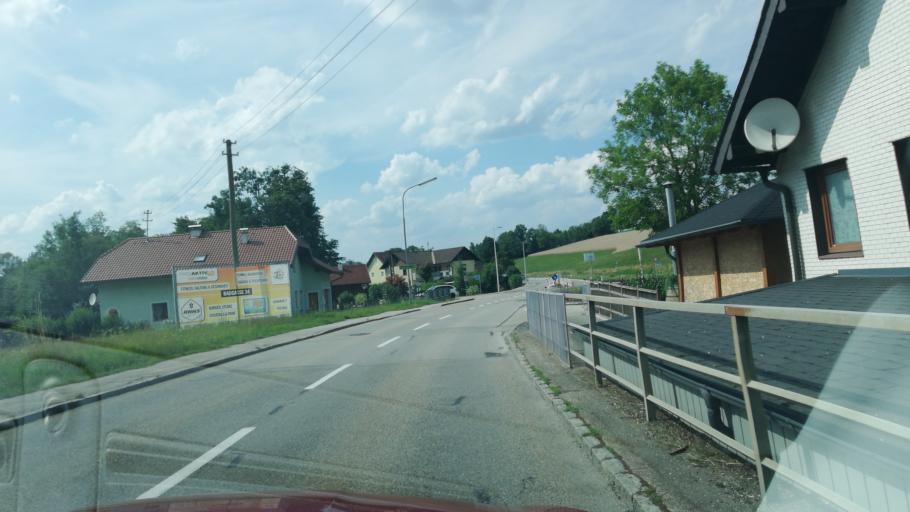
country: AT
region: Upper Austria
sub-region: Politischer Bezirk Vocklabruck
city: Attnang-Puchheim
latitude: 48.0204
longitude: 13.7133
